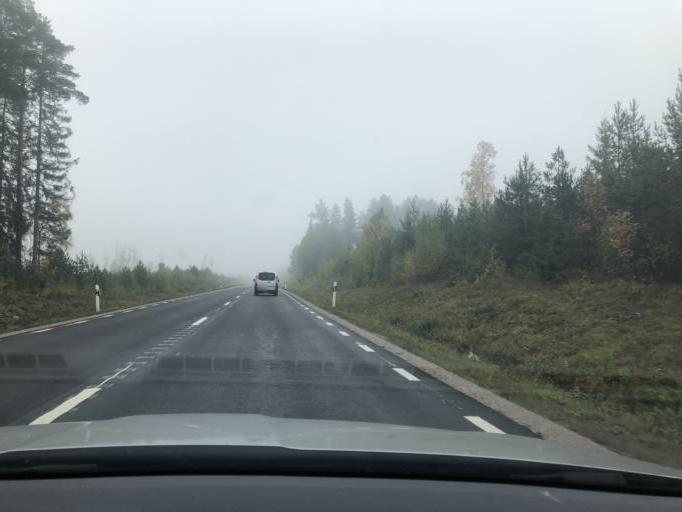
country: SE
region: Uppsala
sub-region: Tierps Kommun
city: Tierp
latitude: 60.3058
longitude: 17.5592
